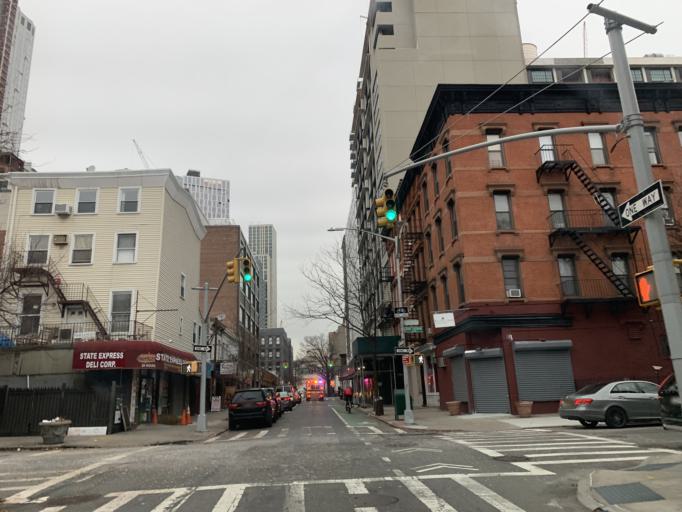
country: US
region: New York
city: New York City
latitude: 40.6874
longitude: -73.9845
